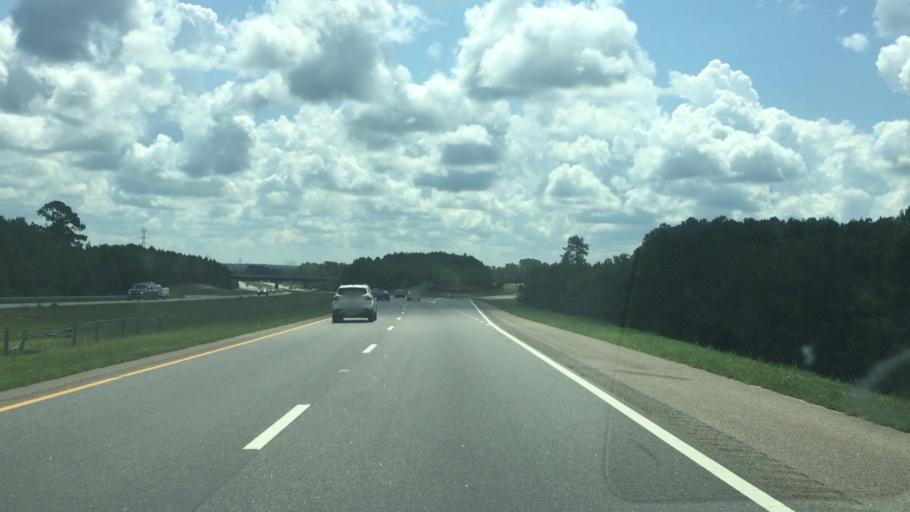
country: US
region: North Carolina
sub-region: Richmond County
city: Cordova
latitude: 34.9339
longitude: -79.8366
